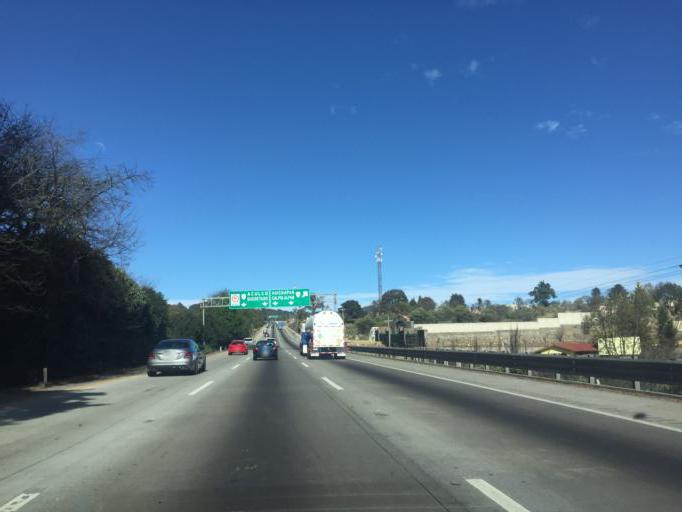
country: MX
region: Mexico
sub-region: Jilotepec
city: San Vicente (Calpulalpan Tercera Manzana)
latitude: 20.0763
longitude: -99.6142
